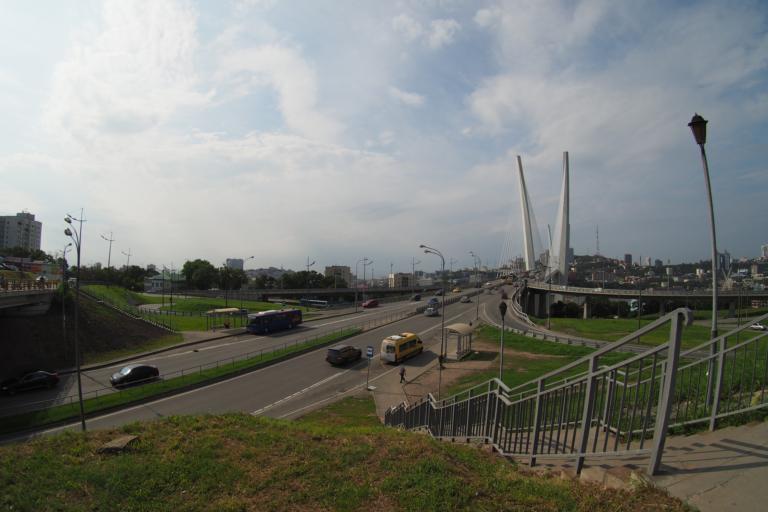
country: RU
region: Primorskiy
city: Vladivostok
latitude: 43.1009
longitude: 131.8965
